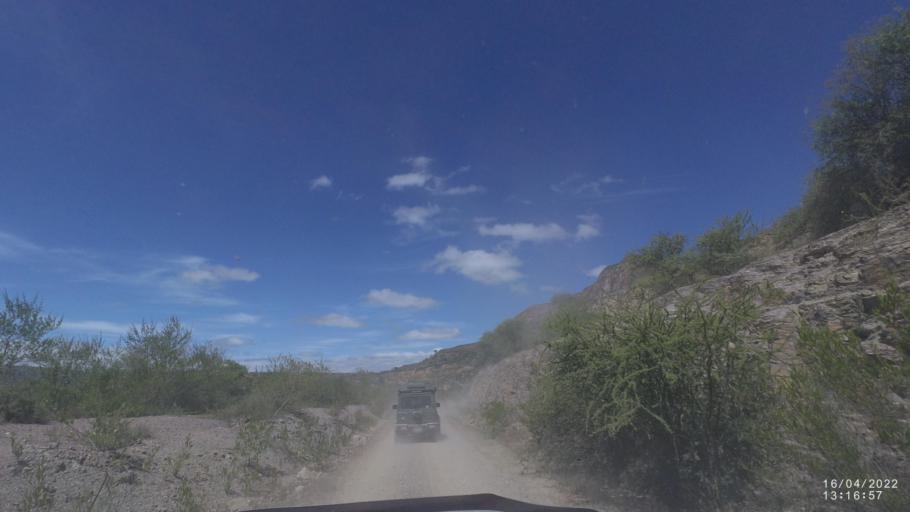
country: BO
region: Cochabamba
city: Mizque
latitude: -17.9868
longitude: -65.6230
